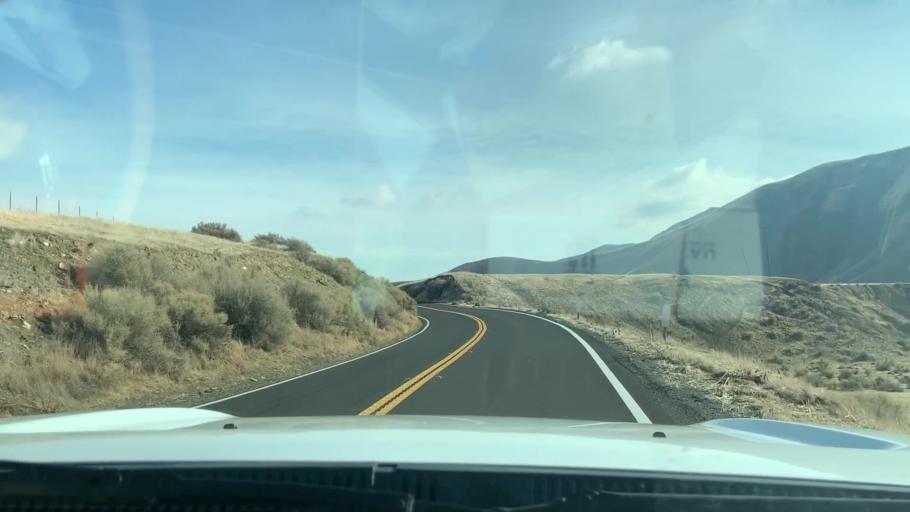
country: US
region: California
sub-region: Fresno County
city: Coalinga
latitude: 36.1013
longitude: -120.4149
